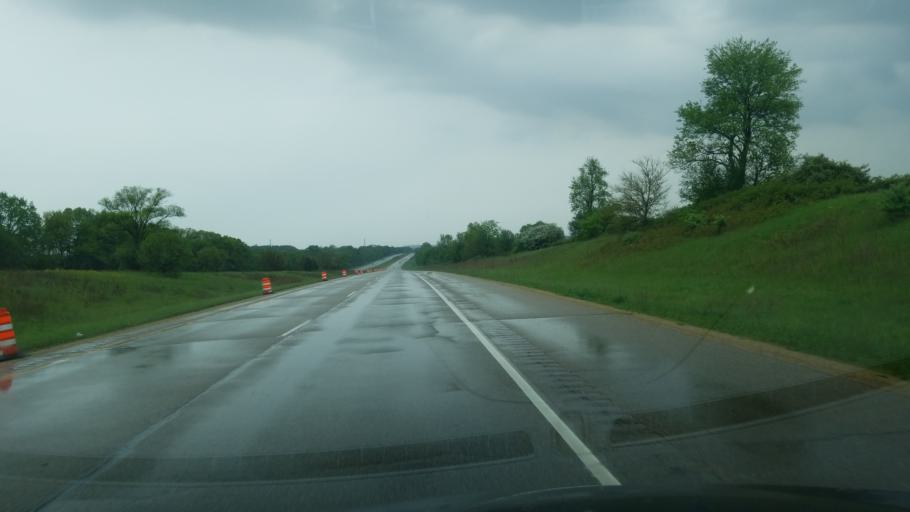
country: US
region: Wisconsin
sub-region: Dane County
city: Oregon
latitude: 42.9774
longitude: -89.3856
